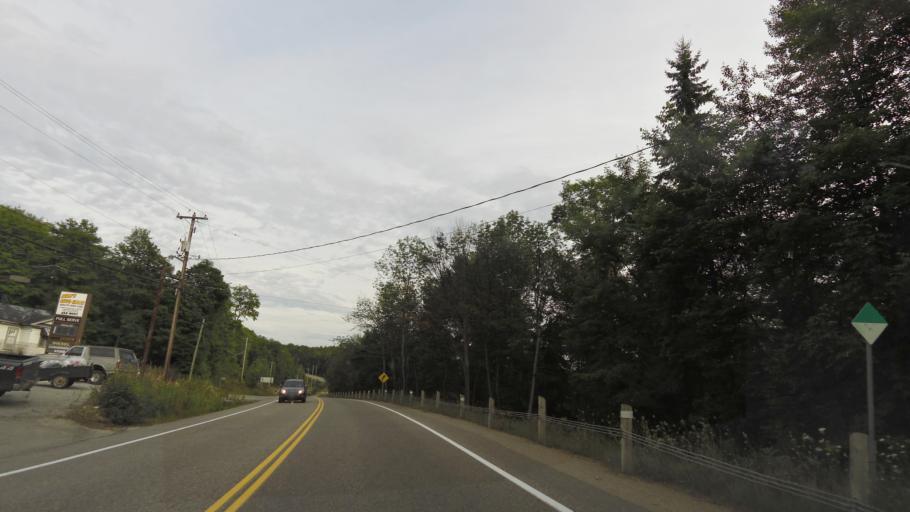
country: CA
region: Ontario
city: Bancroft
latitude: 45.0421
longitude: -78.4881
